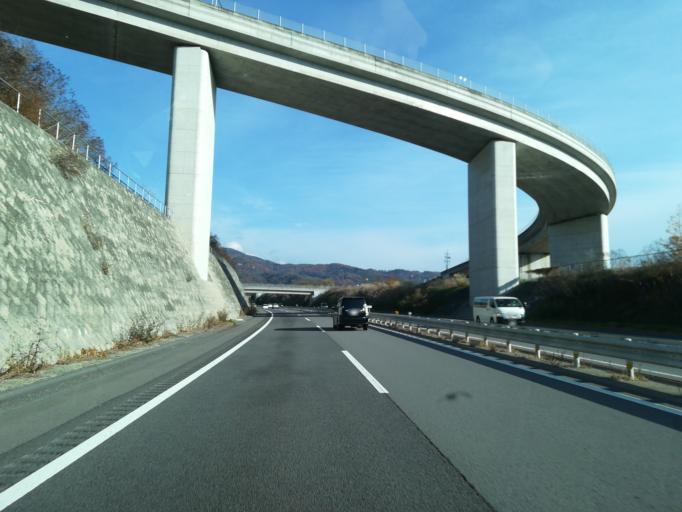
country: JP
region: Nagano
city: Ueda
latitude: 36.4096
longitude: 138.2915
